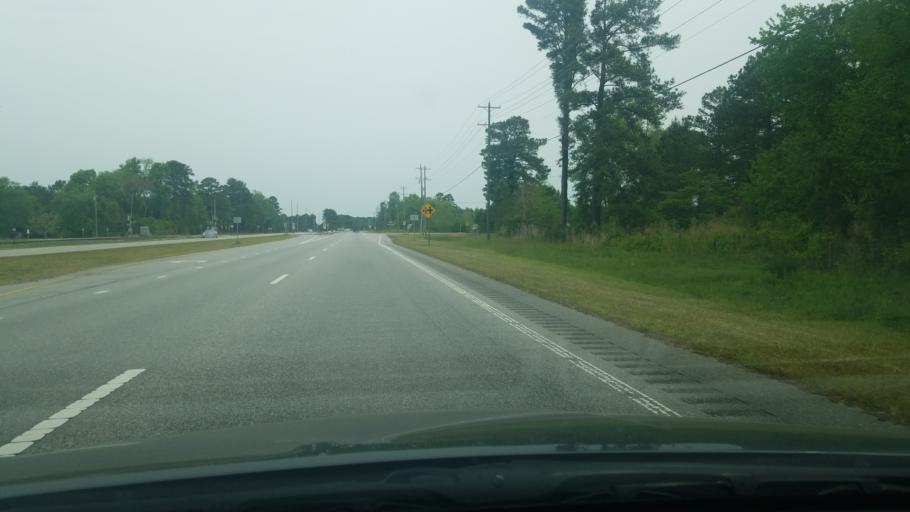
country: US
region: North Carolina
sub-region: Beaufort County
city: Washington
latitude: 35.4682
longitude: -77.1193
